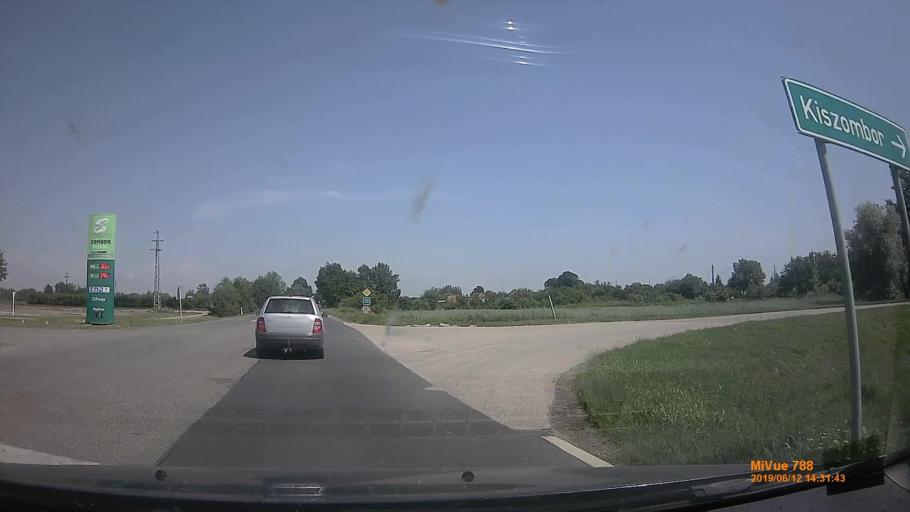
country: HU
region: Csongrad
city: Kiszombor
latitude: 46.1936
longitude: 20.4101
